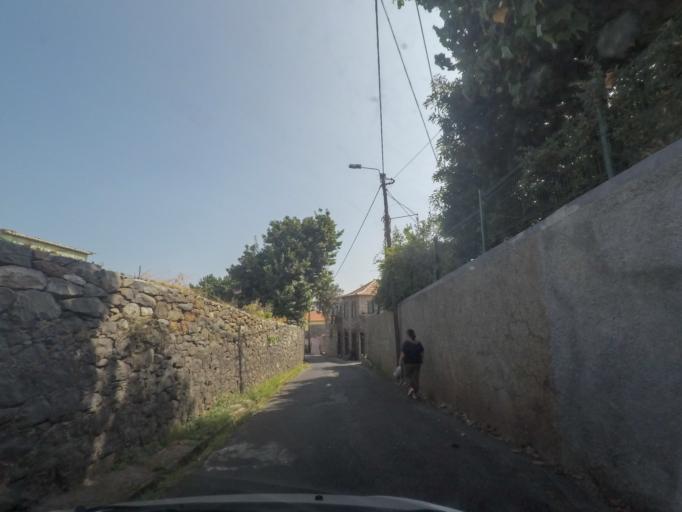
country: PT
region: Madeira
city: Camara de Lobos
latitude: 32.6691
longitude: -16.9494
